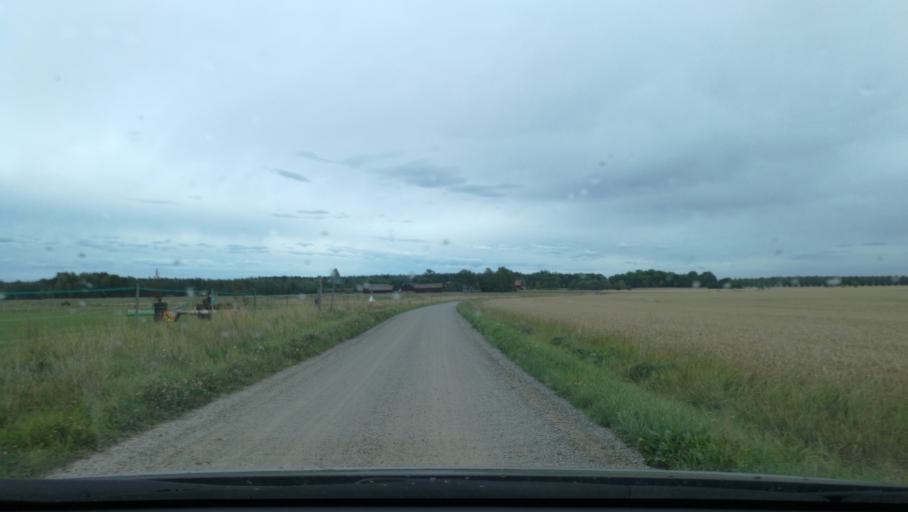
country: SE
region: Vaestmanland
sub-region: Vasteras
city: Tillberga
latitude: 59.7147
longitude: 16.6008
